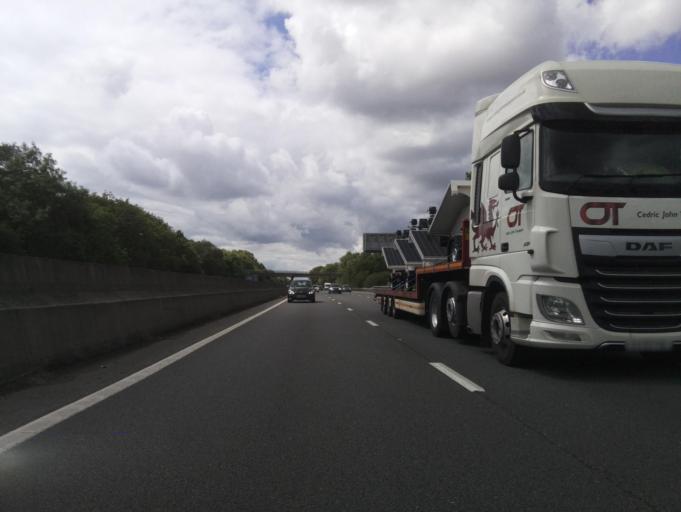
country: GB
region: England
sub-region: Borough of Swindon
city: Chiseldon
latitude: 51.5294
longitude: -1.7472
